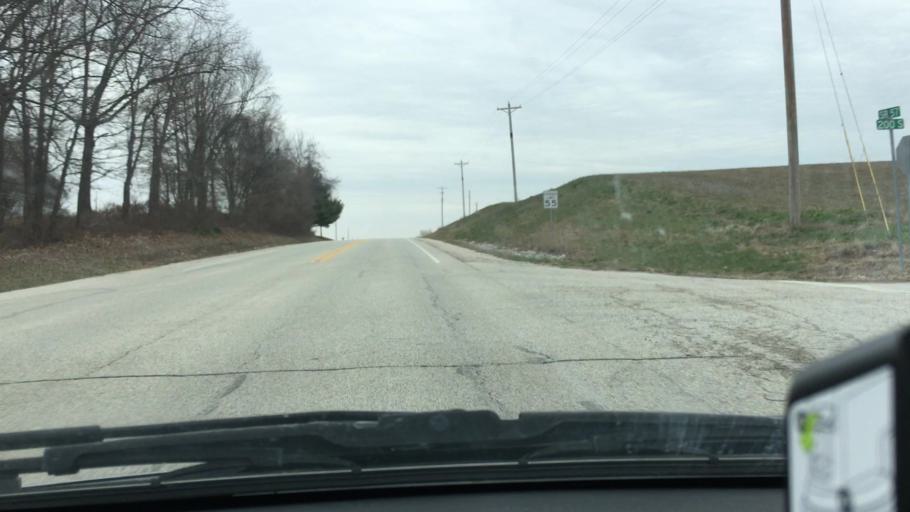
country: US
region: Indiana
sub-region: Greene County
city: Bloomfield
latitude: 38.9944
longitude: -87.0163
